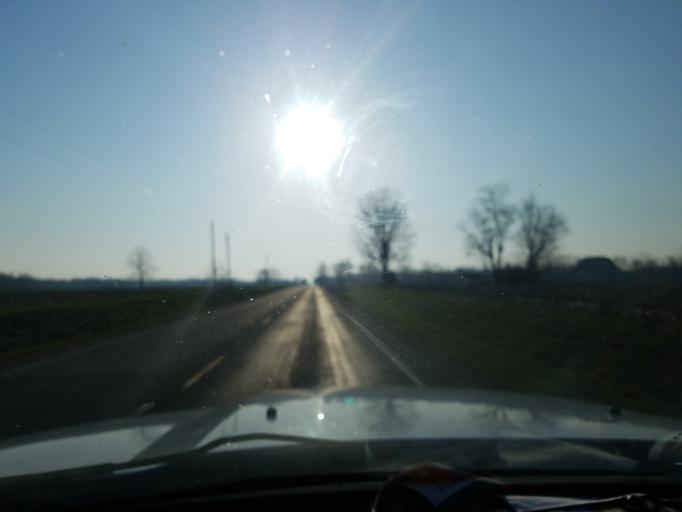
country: US
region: Indiana
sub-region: Vigo County
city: Seelyville
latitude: 39.3886
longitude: -87.1844
